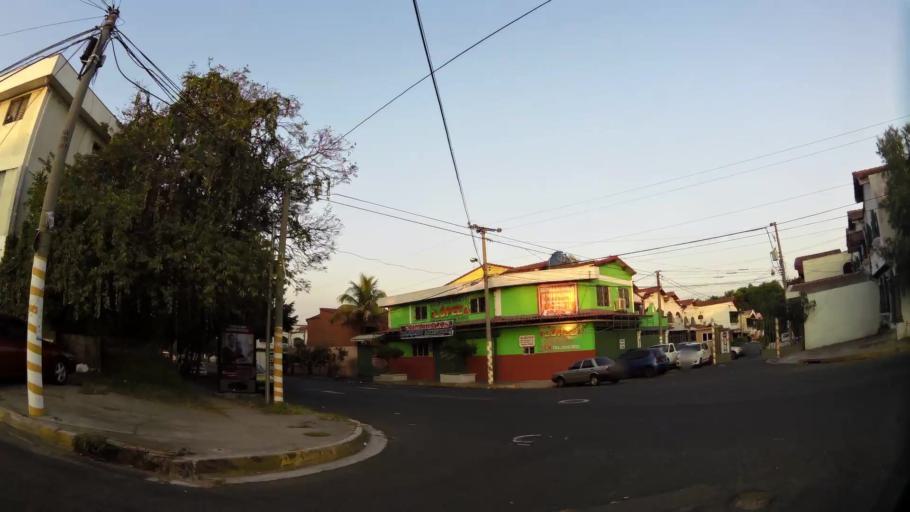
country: SV
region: San Salvador
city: San Salvador
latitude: 13.7073
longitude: -89.2082
